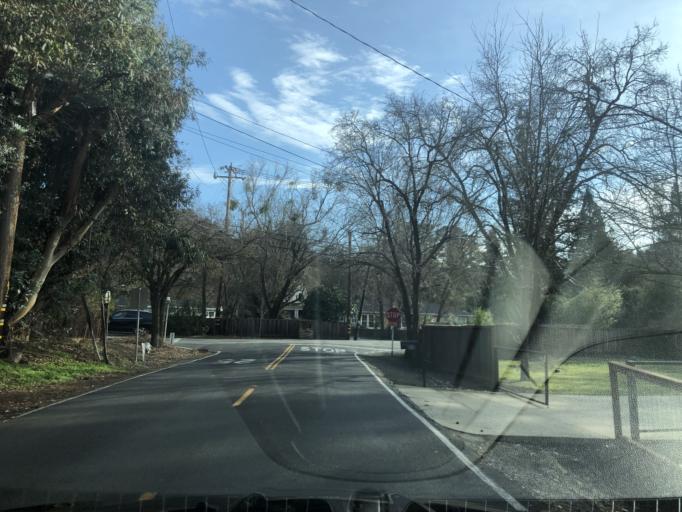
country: US
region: California
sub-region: Contra Costa County
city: Saranap
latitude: 37.8766
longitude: -122.0558
